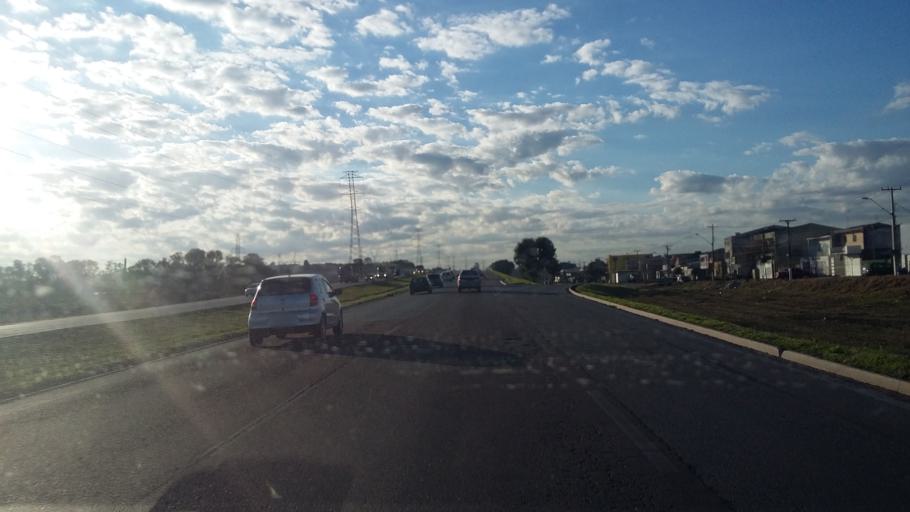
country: BR
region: Parana
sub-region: Araucaria
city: Araucaria
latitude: -25.5198
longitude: -49.3347
